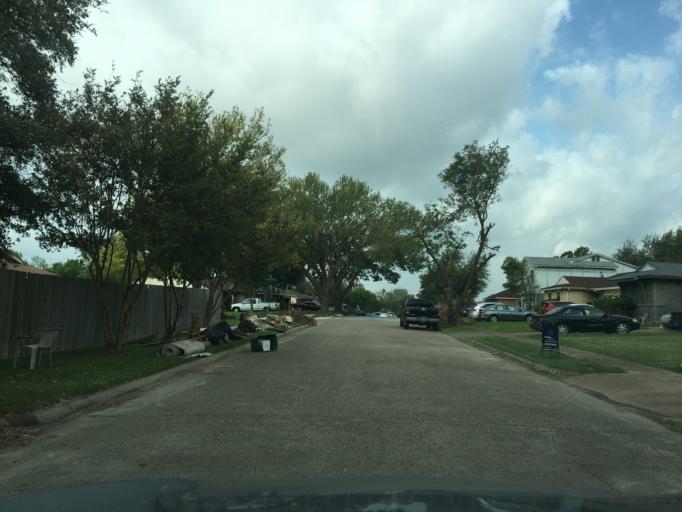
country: US
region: Texas
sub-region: Dallas County
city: Richardson
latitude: 32.9002
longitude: -96.7519
